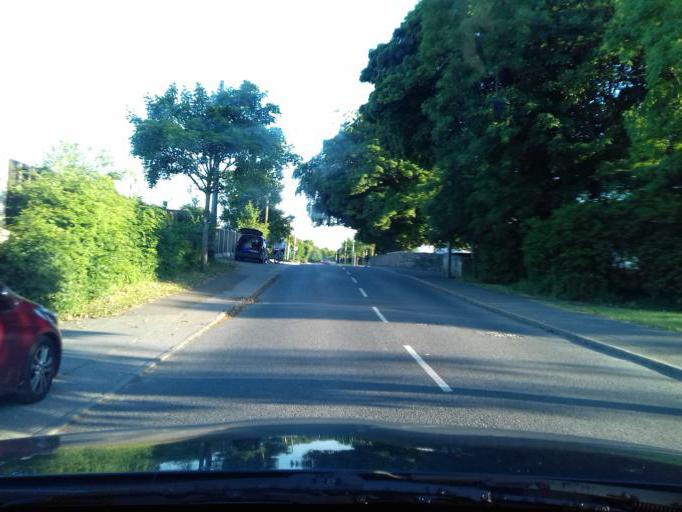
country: IE
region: Leinster
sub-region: An Mhi
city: Ashbourne
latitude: 53.5653
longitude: -6.3841
